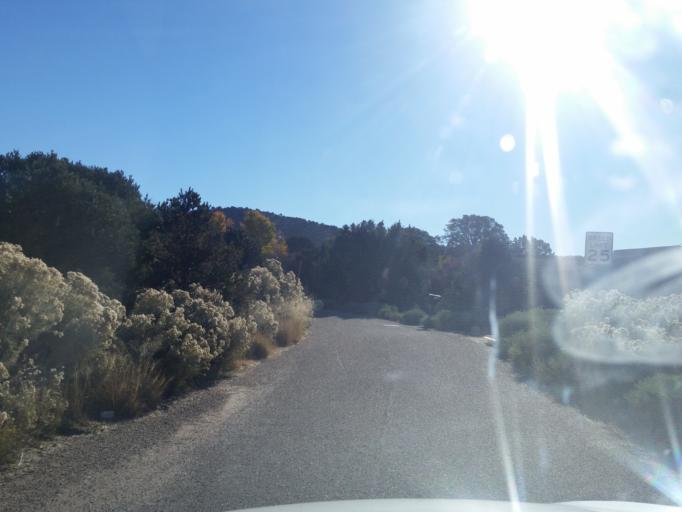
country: US
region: New Mexico
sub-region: Santa Fe County
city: Santa Fe
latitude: 35.6485
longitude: -105.9270
